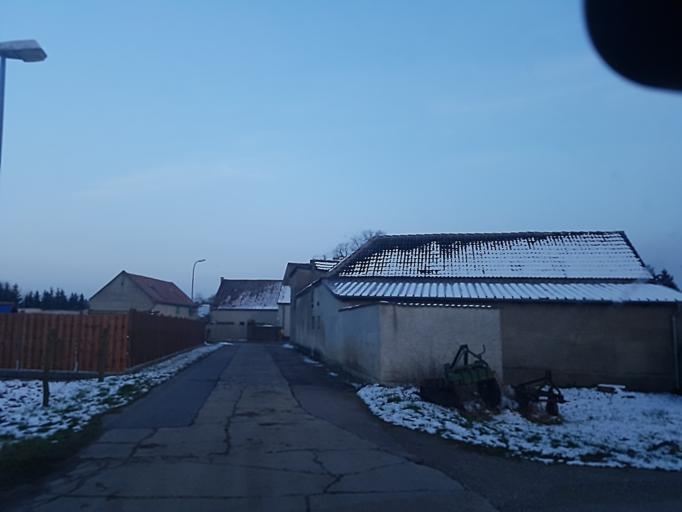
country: DE
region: Brandenburg
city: Muhlberg
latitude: 51.4485
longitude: 13.2312
